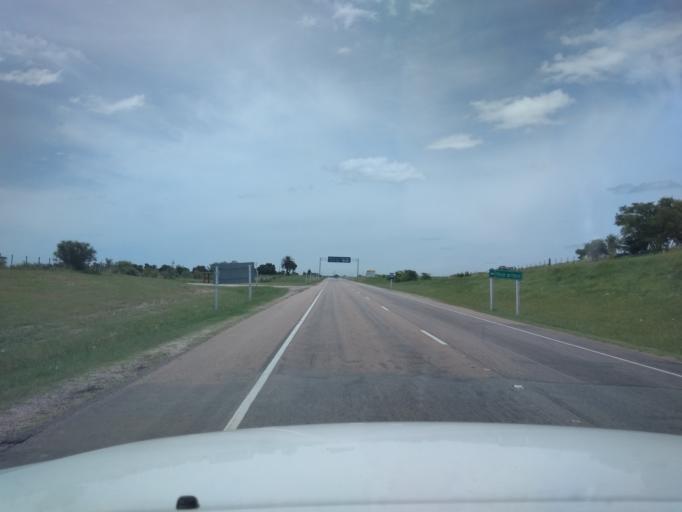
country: UY
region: Florida
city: Cardal
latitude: -34.3233
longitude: -56.2433
